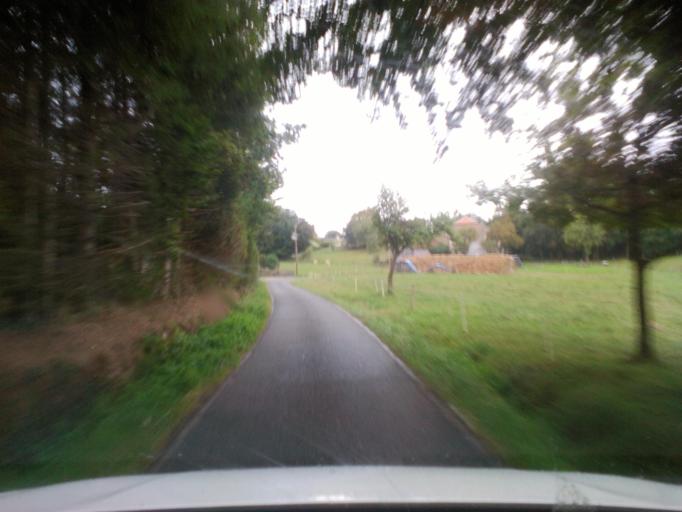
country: FR
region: Lorraine
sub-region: Departement des Vosges
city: Moyenmoutier
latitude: 48.3730
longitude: 6.9368
